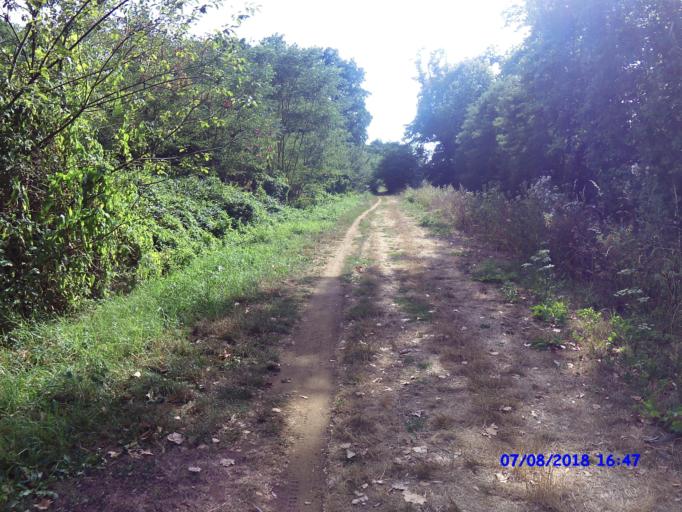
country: BE
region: Flanders
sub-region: Provincie Antwerpen
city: Westerlo
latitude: 51.0843
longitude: 4.9201
